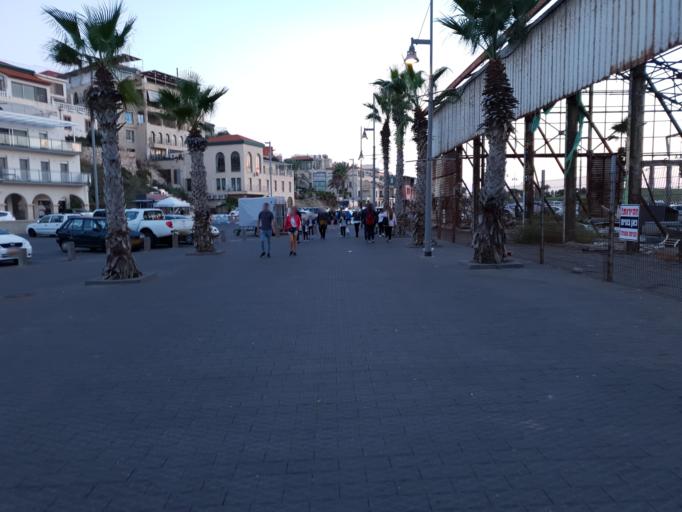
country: IL
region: Tel Aviv
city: Yafo
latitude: 32.0508
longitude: 34.7492
